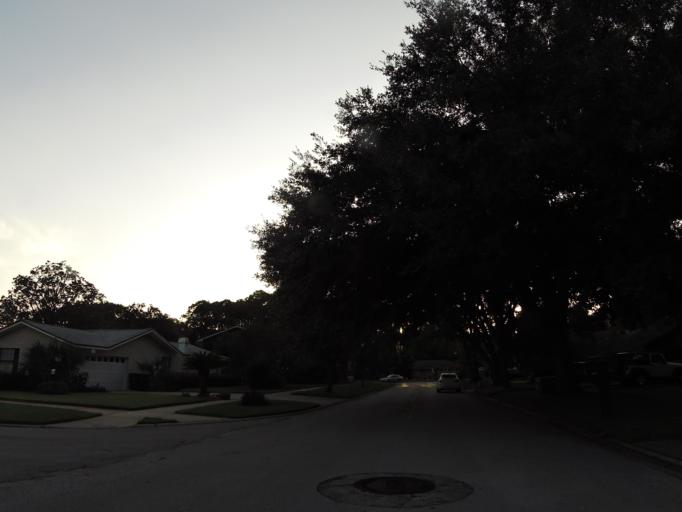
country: US
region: Florida
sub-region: Clay County
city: Orange Park
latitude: 30.2022
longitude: -81.6228
